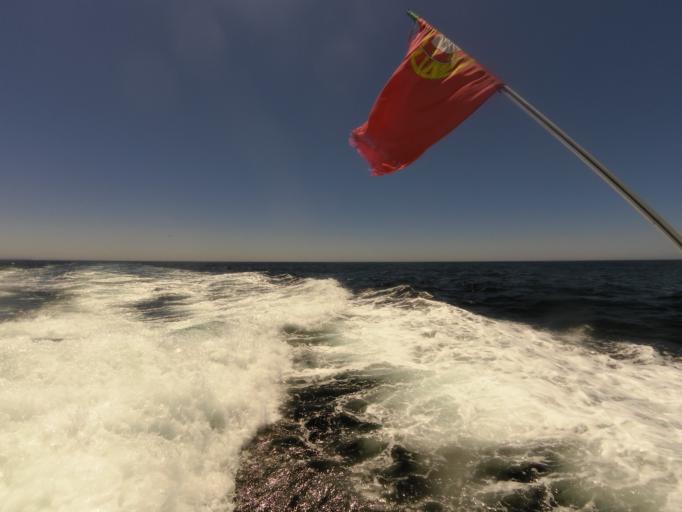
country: PT
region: Leiria
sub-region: Peniche
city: Peniche
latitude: 39.4106
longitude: -9.5023
